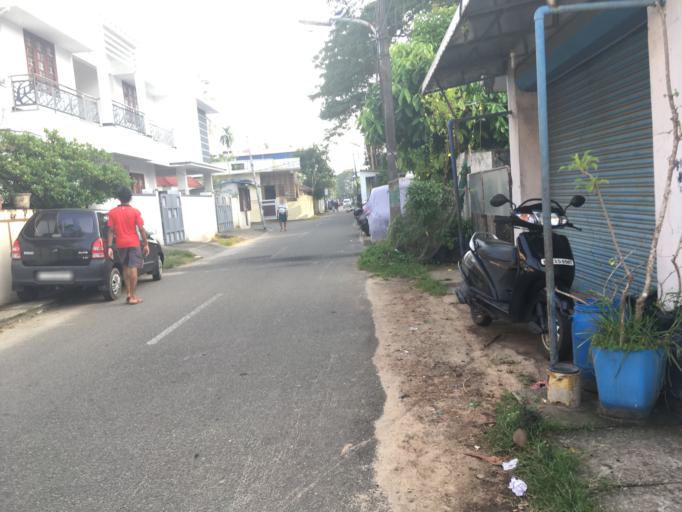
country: IN
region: Kerala
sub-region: Ernakulam
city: Cochin
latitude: 9.9578
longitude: 76.2405
